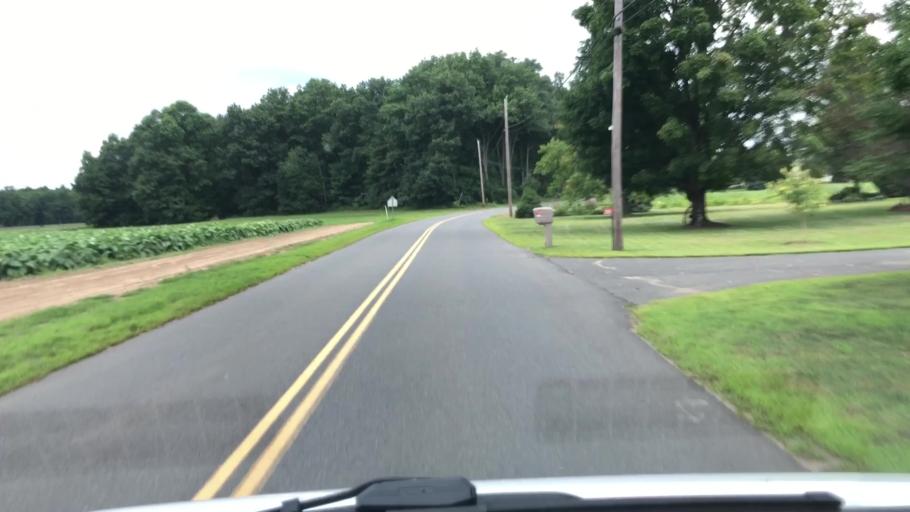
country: US
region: Massachusetts
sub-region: Franklin County
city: South Deerfield
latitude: 42.4524
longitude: -72.6085
